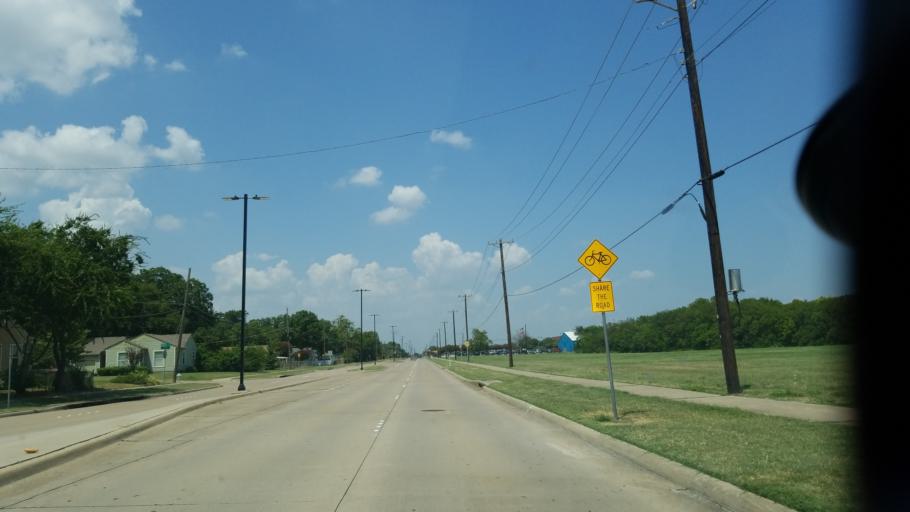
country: US
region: Texas
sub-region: Dallas County
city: Garland
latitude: 32.9180
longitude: -96.6395
